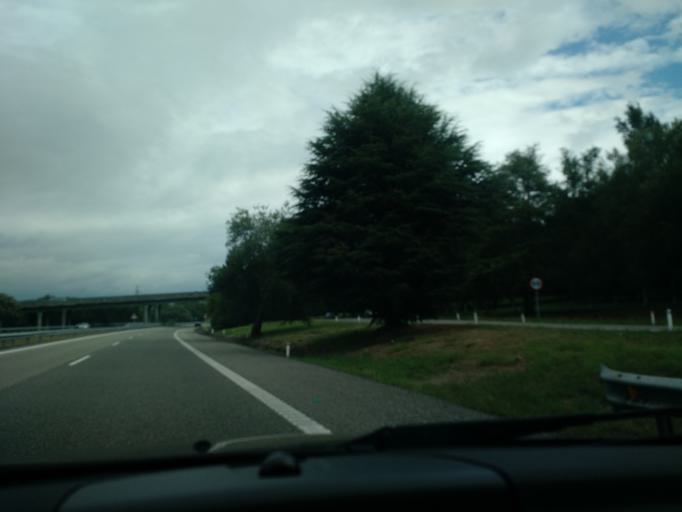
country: ES
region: Galicia
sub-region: Provincia da Coruna
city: Betanzos
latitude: 43.2596
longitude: -8.2542
